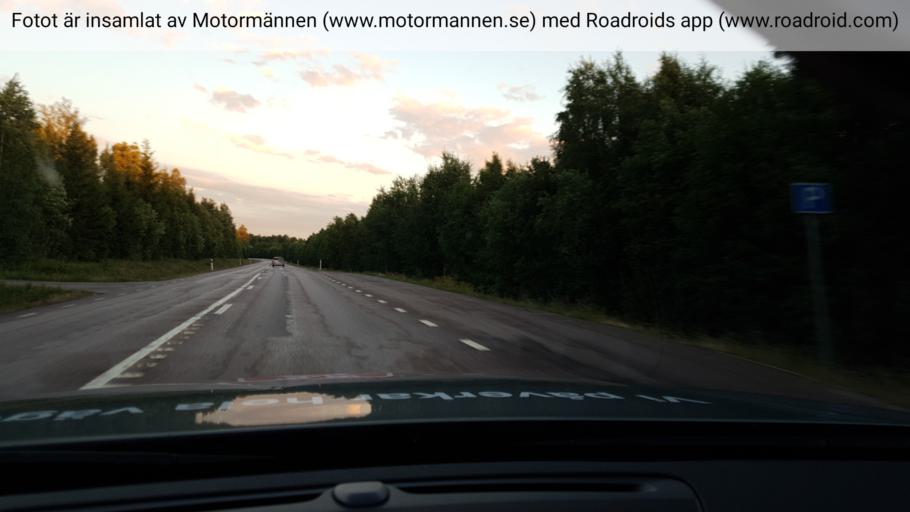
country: SE
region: Vaestmanland
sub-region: Skinnskattebergs Kommun
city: Skinnskatteberg
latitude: 59.9202
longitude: 15.7148
